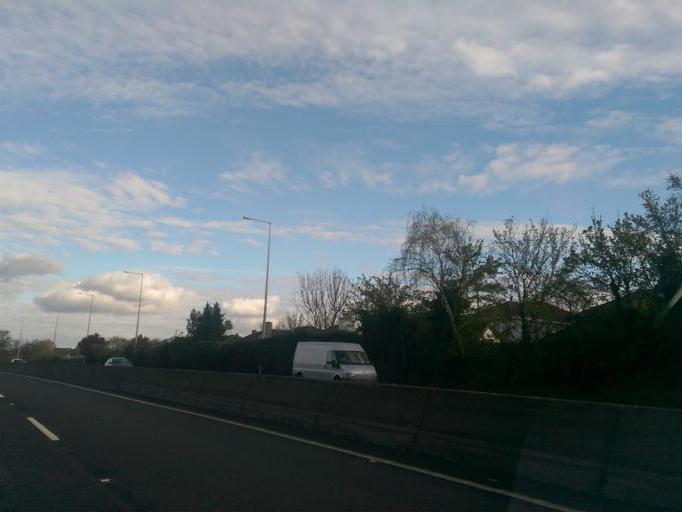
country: IE
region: Leinster
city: Lucan
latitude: 53.3527
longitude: -6.4561
